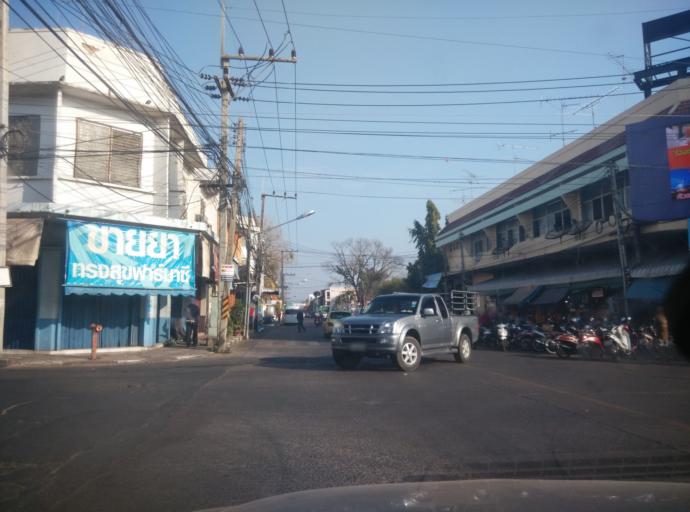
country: TH
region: Sisaket
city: Si Sa Ket
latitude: 15.1164
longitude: 104.3297
